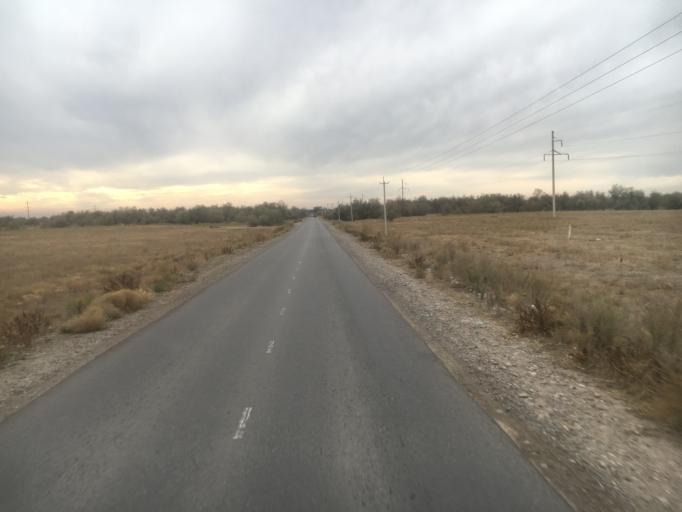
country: KZ
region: Almaty Oblysy
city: Energeticheskiy
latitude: 43.5856
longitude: 77.0833
